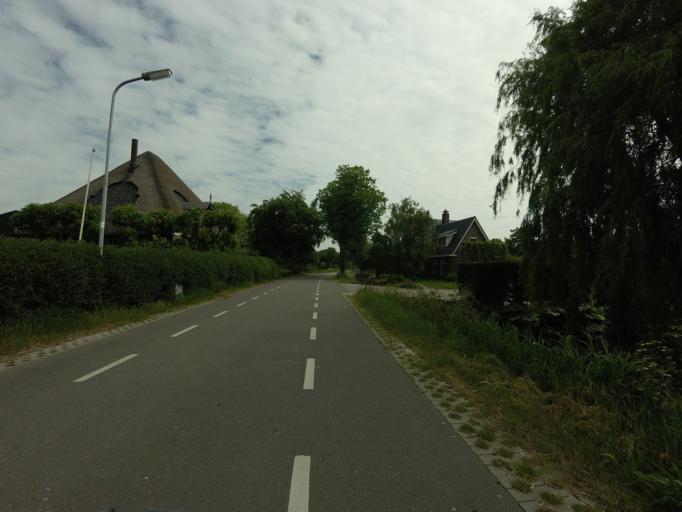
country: NL
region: North Holland
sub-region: Gemeente Medemblik
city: Opperdoes
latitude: 52.6997
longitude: 5.0861
